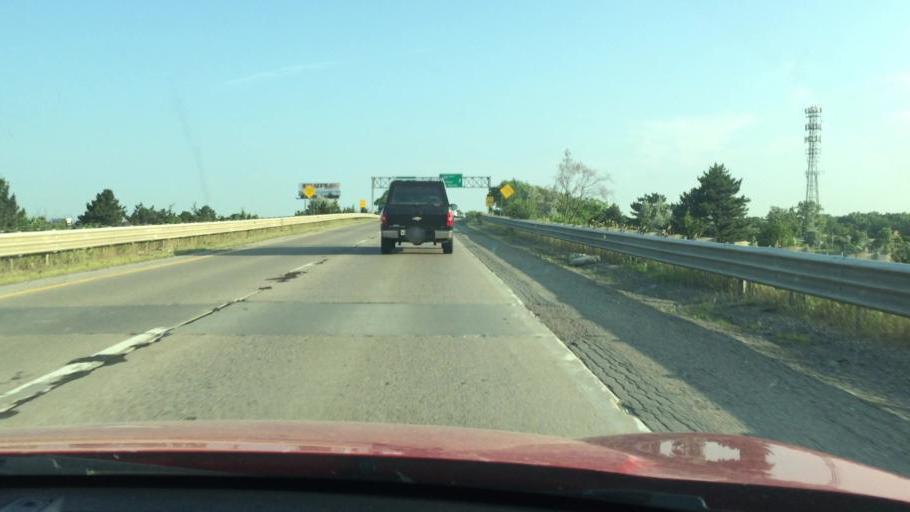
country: US
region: Michigan
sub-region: Genesee County
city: Flint
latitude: 42.9804
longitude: -83.7280
